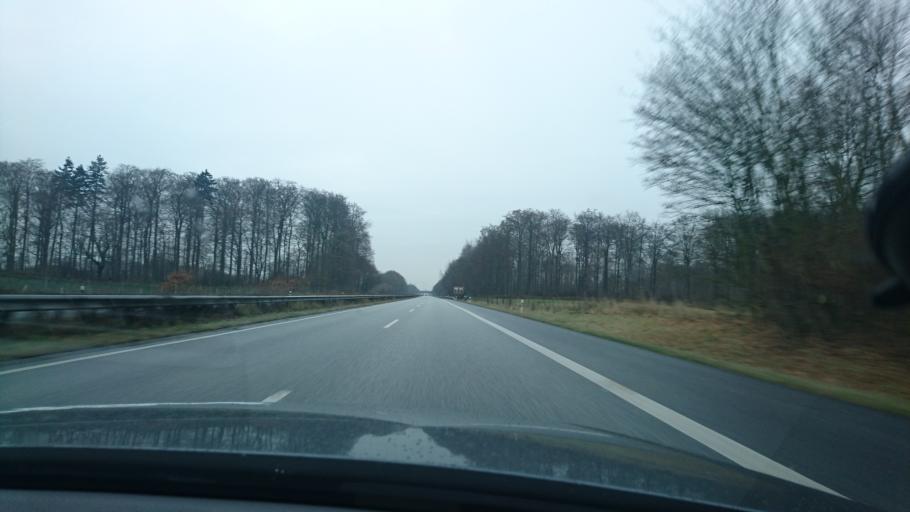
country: DE
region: Schleswig-Holstein
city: Manhagen
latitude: 54.1888
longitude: 10.8957
